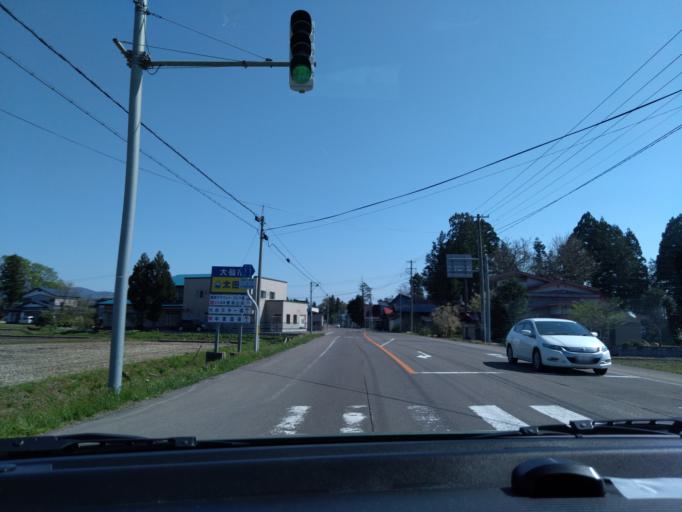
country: JP
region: Akita
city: Kakunodatemachi
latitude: 39.5325
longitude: 140.5854
